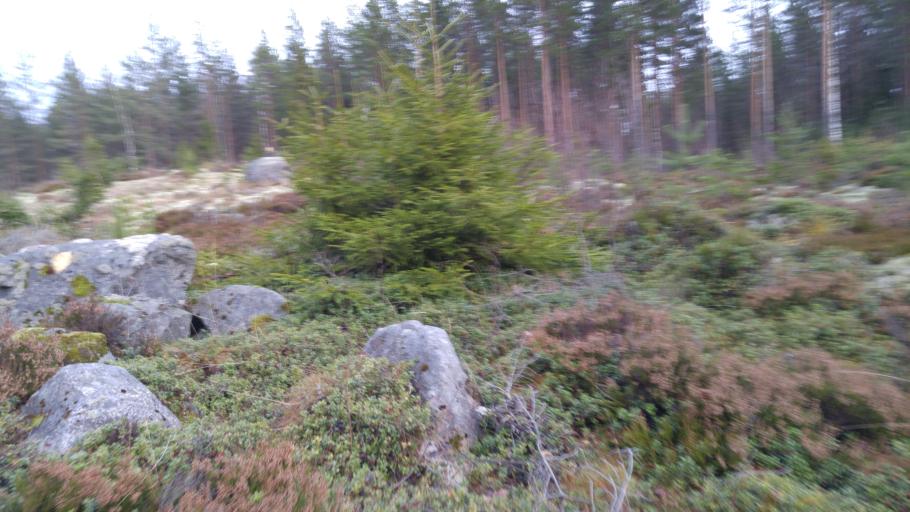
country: FI
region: Pirkanmaa
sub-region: Tampere
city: Kangasala
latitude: 61.6028
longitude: 23.9763
